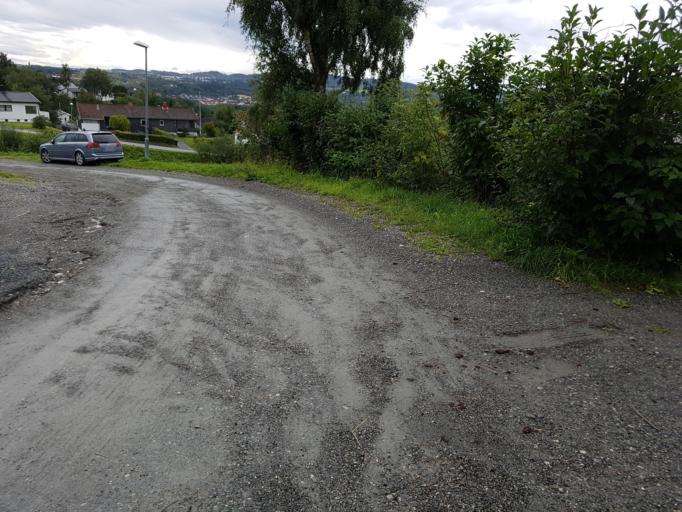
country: NO
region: Sor-Trondelag
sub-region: Trondheim
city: Trondheim
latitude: 63.3931
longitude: 10.4185
